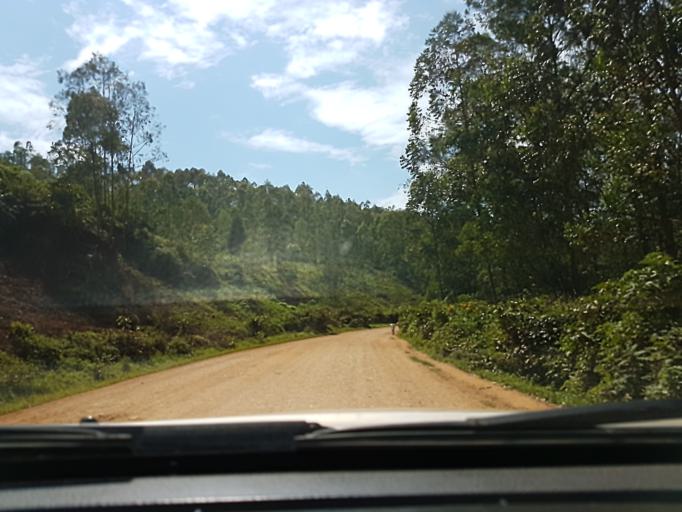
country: CD
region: South Kivu
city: Bukavu
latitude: -2.6469
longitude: 28.8732
